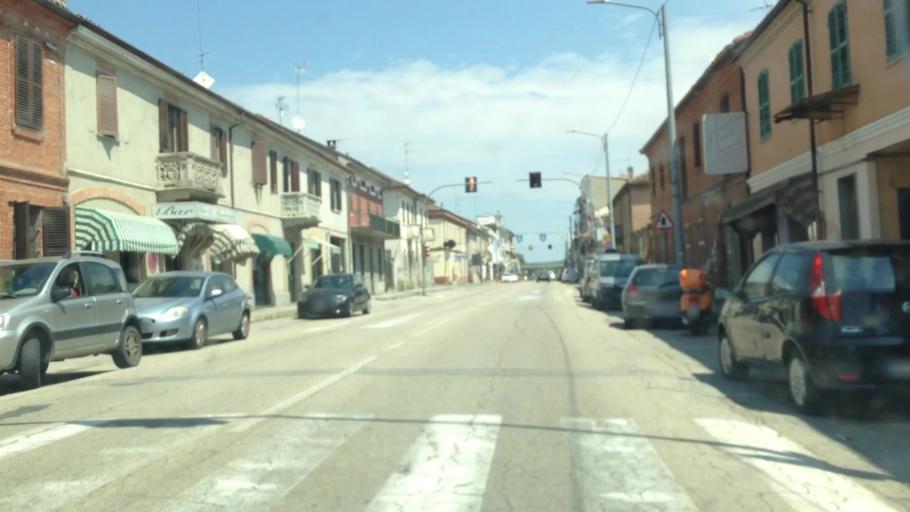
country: IT
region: Piedmont
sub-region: Provincia di Asti
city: Castell'Alfero
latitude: 44.9560
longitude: 8.2231
